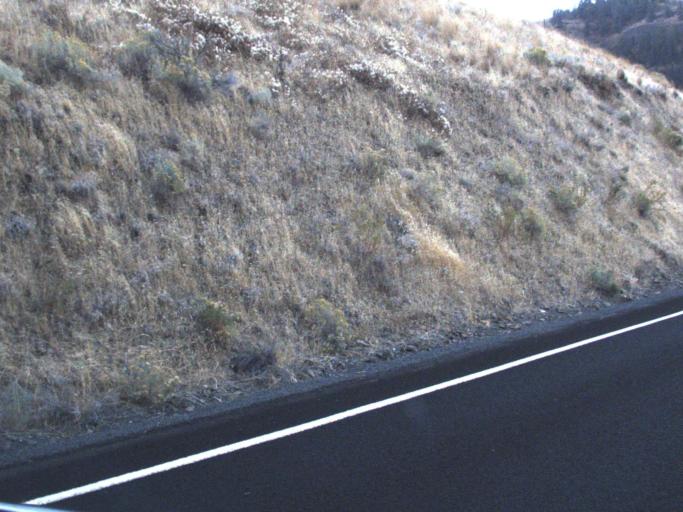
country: US
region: Washington
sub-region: Okanogan County
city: Coulee Dam
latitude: 47.8805
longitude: -118.7190
